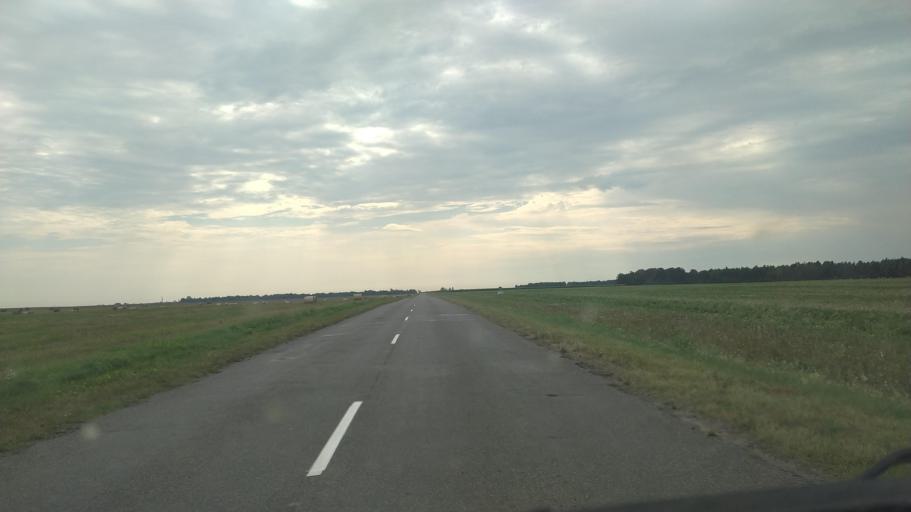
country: BY
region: Brest
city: Byaroza
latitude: 52.5738
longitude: 24.8777
